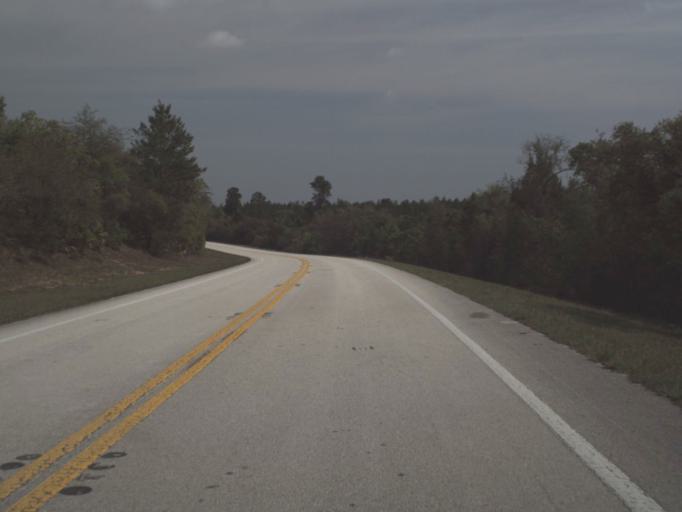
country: US
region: Florida
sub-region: Lake County
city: Astor
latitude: 29.2185
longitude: -81.6468
